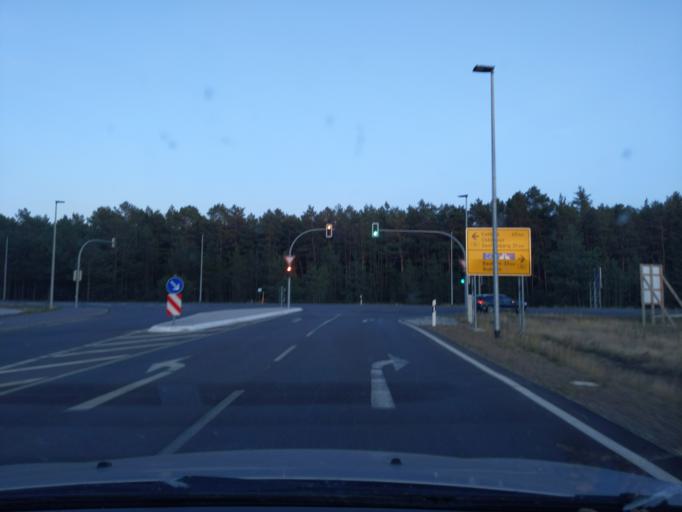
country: DE
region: Saxony
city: Hoyerswerda
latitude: 51.4286
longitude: 14.2997
